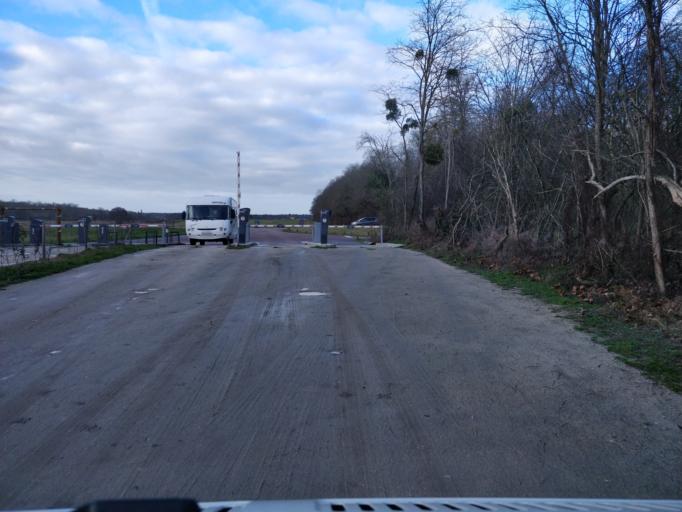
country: FR
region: Centre
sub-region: Departement du Loir-et-Cher
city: Saint-Dye-sur-Loire
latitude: 47.6189
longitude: 1.5090
